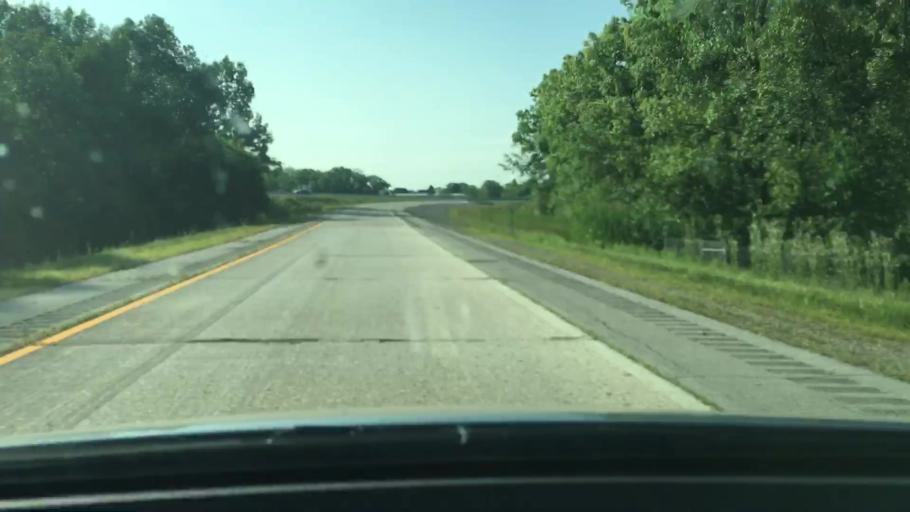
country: US
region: Wisconsin
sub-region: Brown County
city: Ashwaubenon
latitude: 44.4833
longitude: -88.0825
